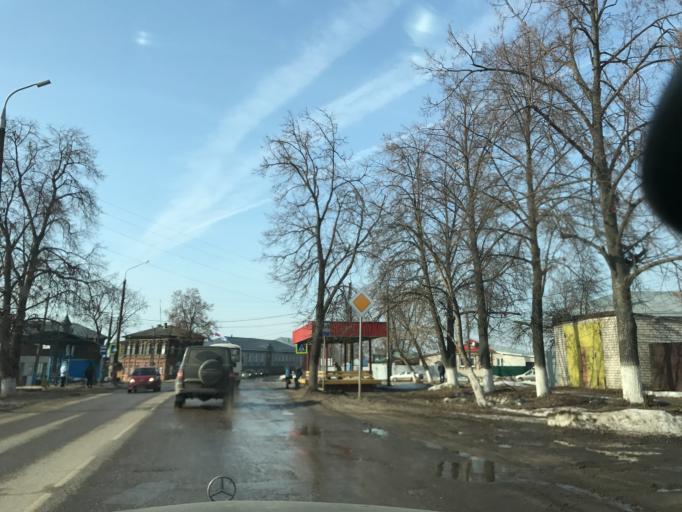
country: RU
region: Nizjnij Novgorod
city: Pavlovo
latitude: 55.9649
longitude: 43.0811
